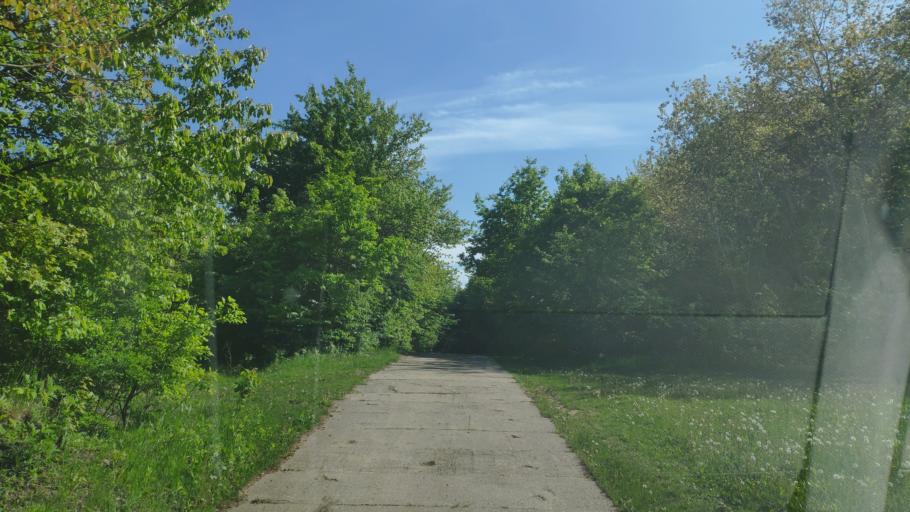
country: SK
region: Kosicky
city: Secovce
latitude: 48.6951
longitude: 21.5969
